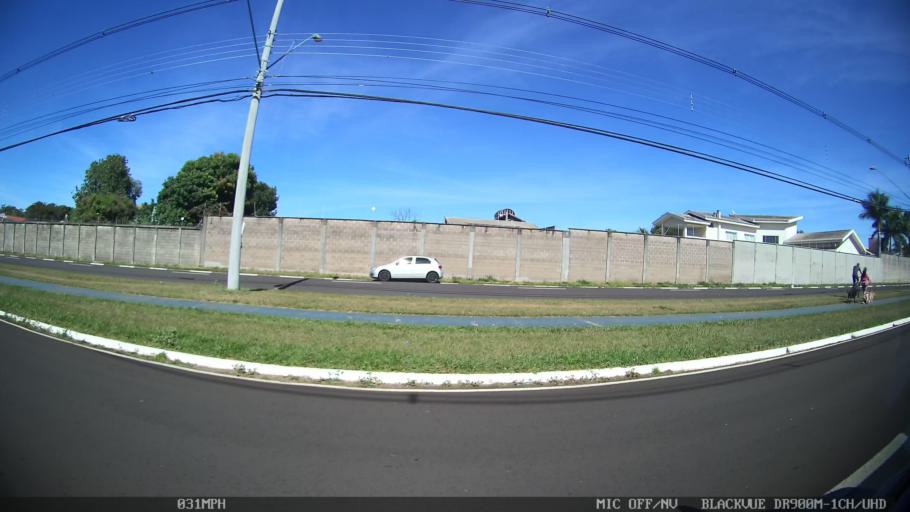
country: BR
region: Sao Paulo
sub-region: Franca
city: Franca
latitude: -20.5628
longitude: -47.3675
